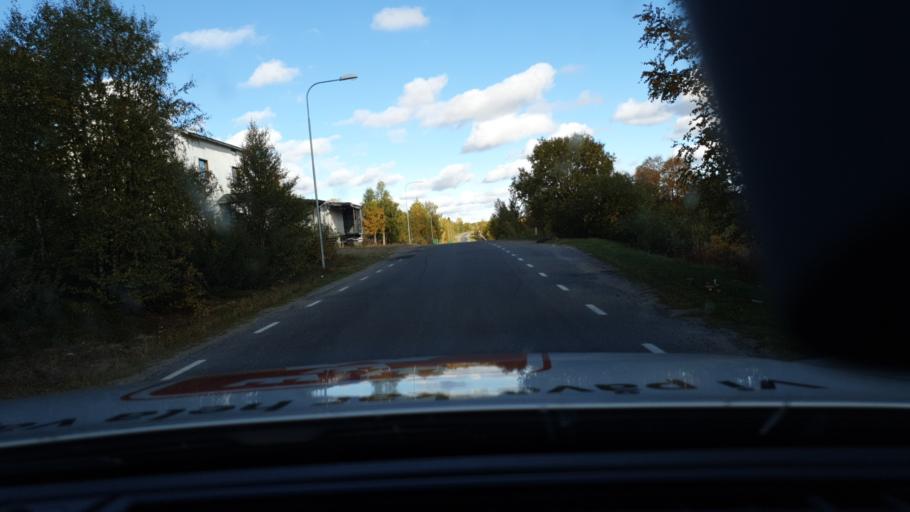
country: NO
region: Finnmark Fylke
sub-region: Kautokeino
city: Kautokeino
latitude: 68.3766
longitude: 22.8054
